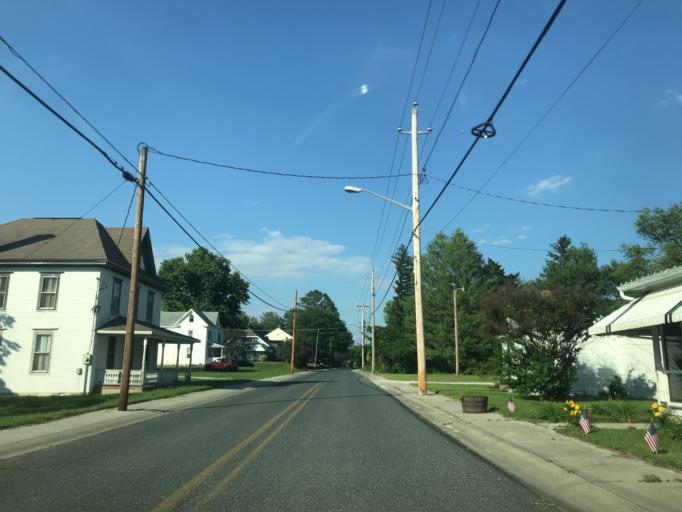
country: US
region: Maryland
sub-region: Wicomico County
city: Hebron
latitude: 38.5369
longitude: -75.7210
